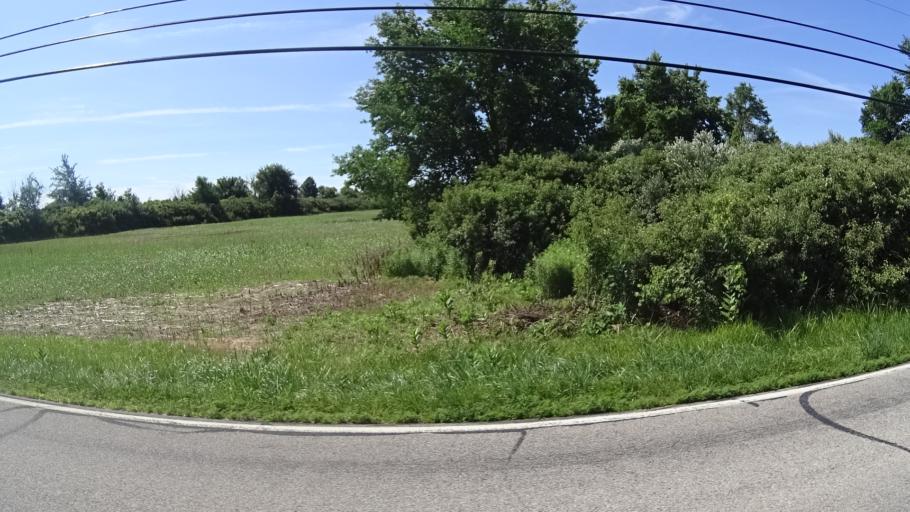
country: US
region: Ohio
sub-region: Ottawa County
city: Port Clinton
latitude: 41.4332
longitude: -82.8786
